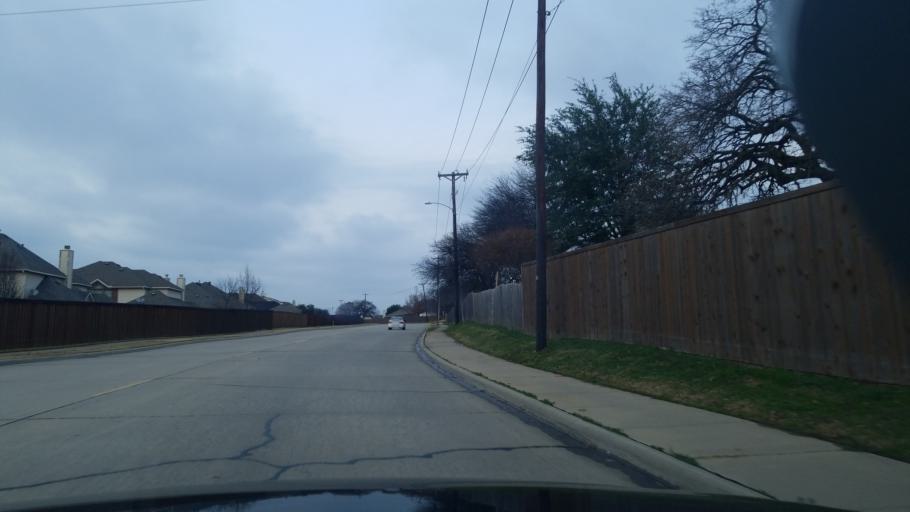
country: US
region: Texas
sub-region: Denton County
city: Corinth
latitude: 33.1373
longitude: -97.0892
